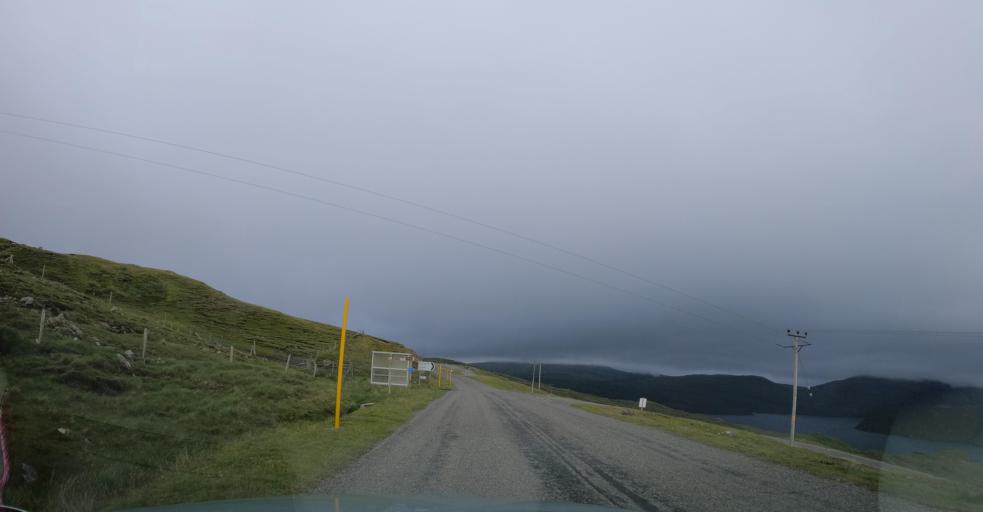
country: GB
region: Scotland
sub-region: Eilean Siar
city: Harris
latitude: 57.9585
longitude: -6.7482
